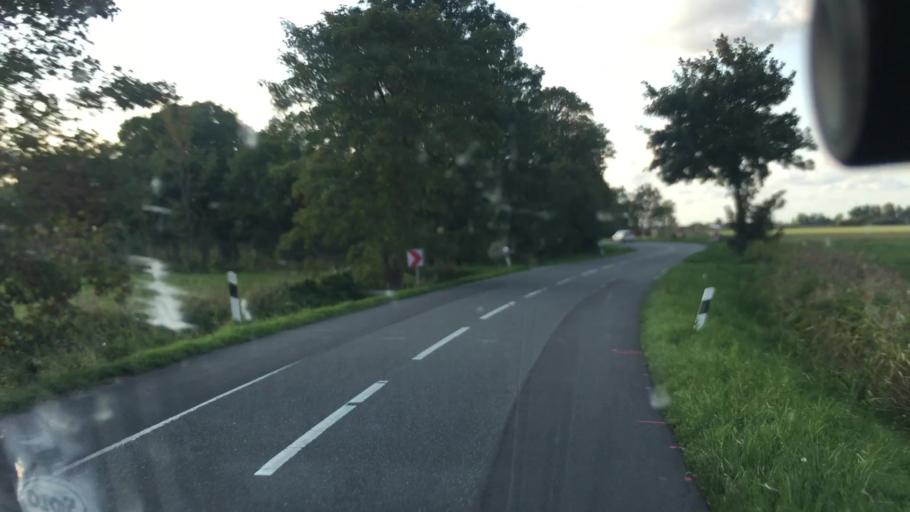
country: DE
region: Lower Saxony
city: Wittmund
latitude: 53.6405
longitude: 7.8186
